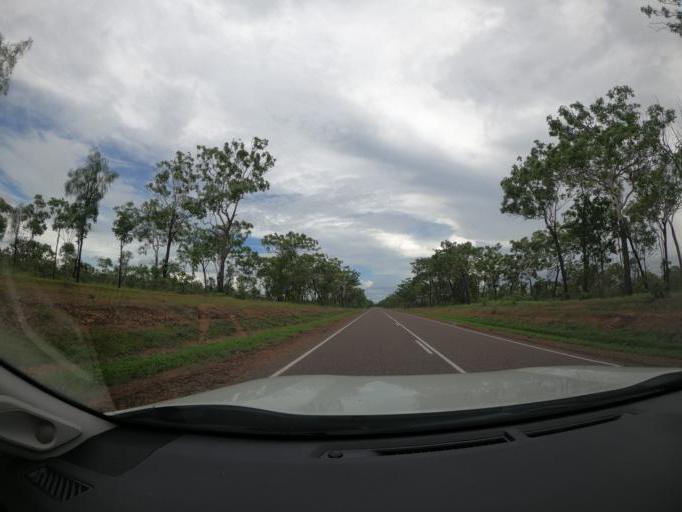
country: AU
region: Northern Territory
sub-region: Litchfield
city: McMinns Lagoon
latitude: -12.8303
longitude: 131.8825
